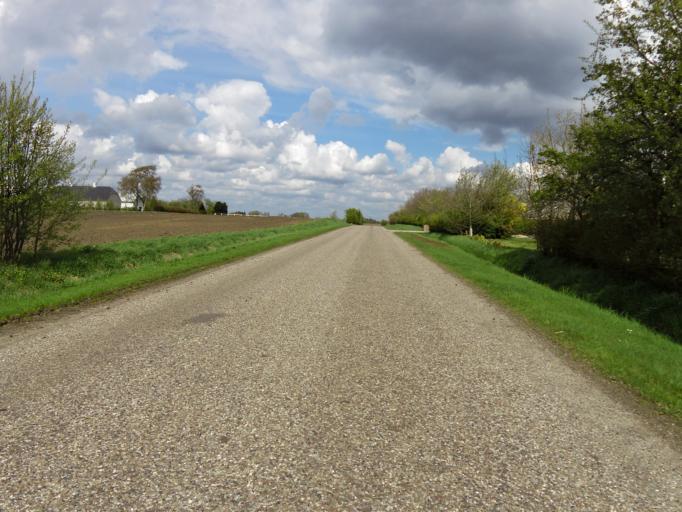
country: DK
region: South Denmark
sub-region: Tonder Kommune
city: Toftlund
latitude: 55.2053
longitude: 9.1315
